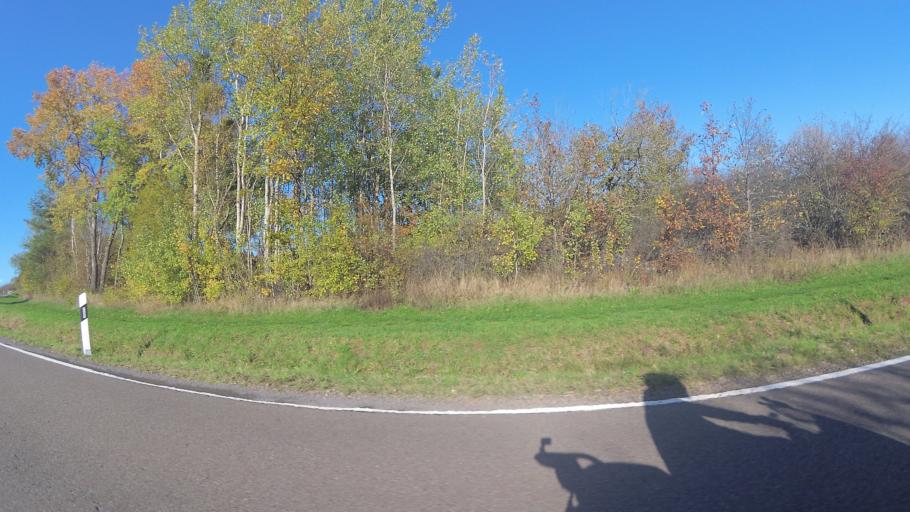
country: DE
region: Saarland
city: Britten
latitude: 49.5275
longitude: 6.7005
